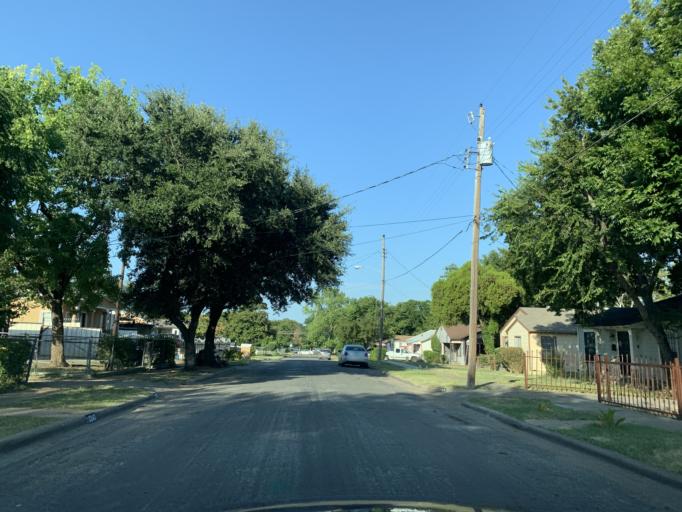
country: US
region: Texas
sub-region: Dallas County
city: Dallas
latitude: 32.7086
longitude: -96.7930
